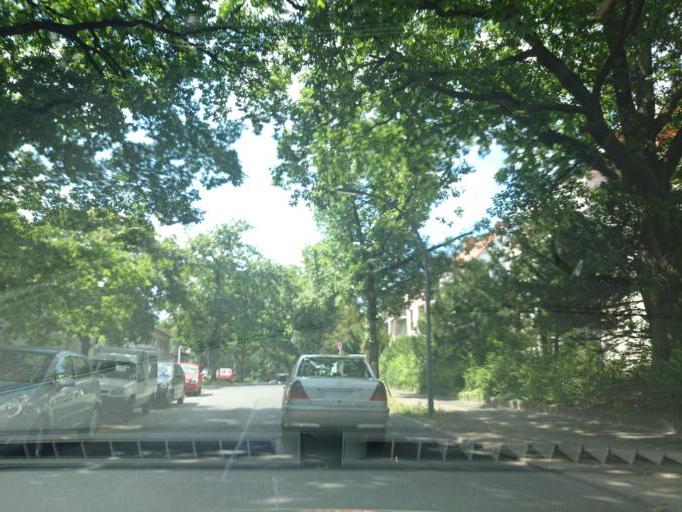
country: DE
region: Berlin
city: Nikolassee
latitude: 52.4347
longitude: 13.1966
